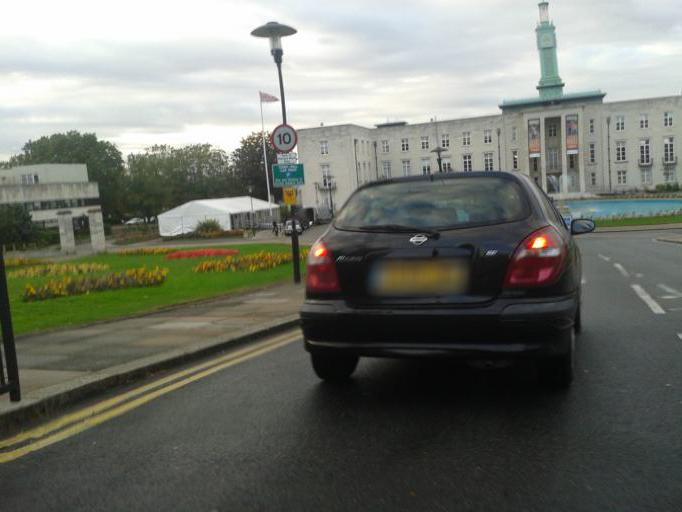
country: GB
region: England
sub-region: Greater London
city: Walthamstow
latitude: 51.5901
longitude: -0.0133
